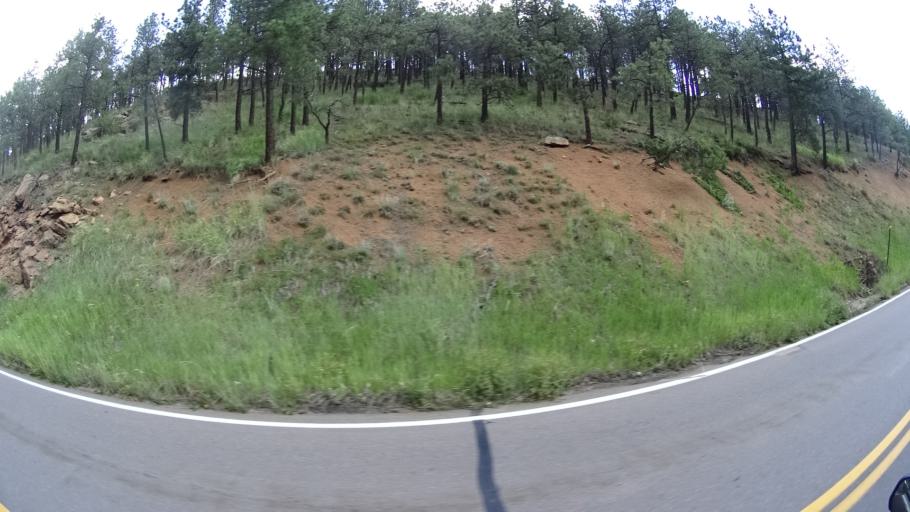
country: US
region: Colorado
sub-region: El Paso County
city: Cascade-Chipita Park
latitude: 38.9106
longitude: -105.0186
